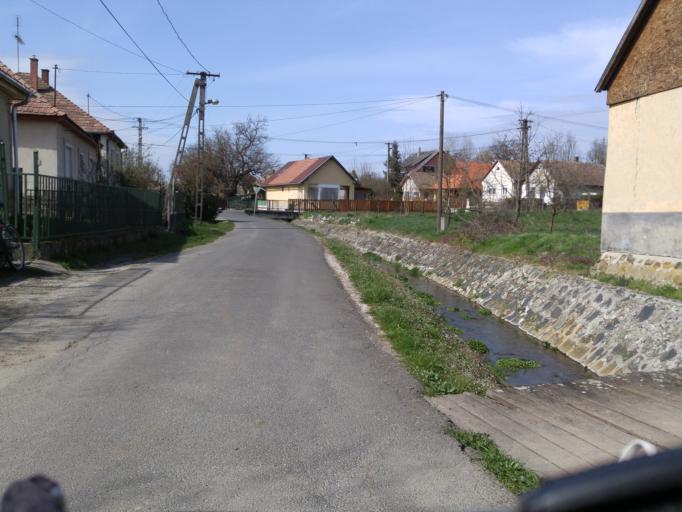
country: HU
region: Nograd
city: Retsag
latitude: 47.9252
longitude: 19.1741
